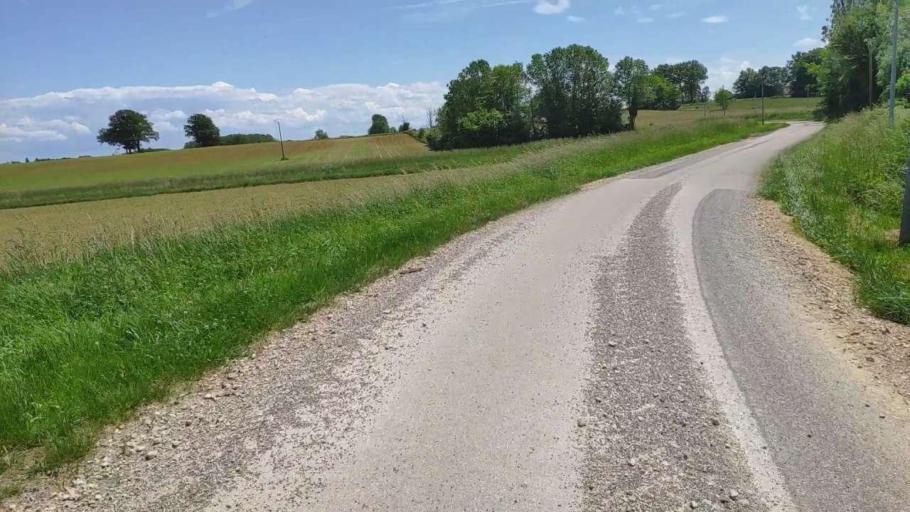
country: FR
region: Franche-Comte
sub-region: Departement du Jura
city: Bletterans
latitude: 46.7893
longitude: 5.3778
